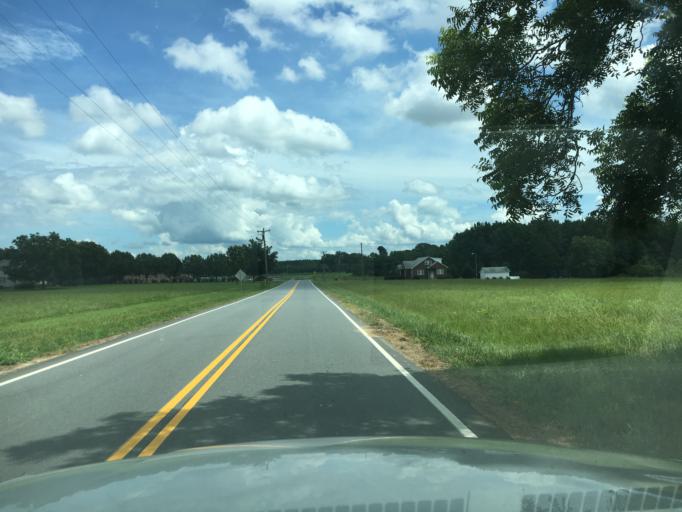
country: US
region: South Carolina
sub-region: Anderson County
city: Belton
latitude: 34.5383
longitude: -82.4410
